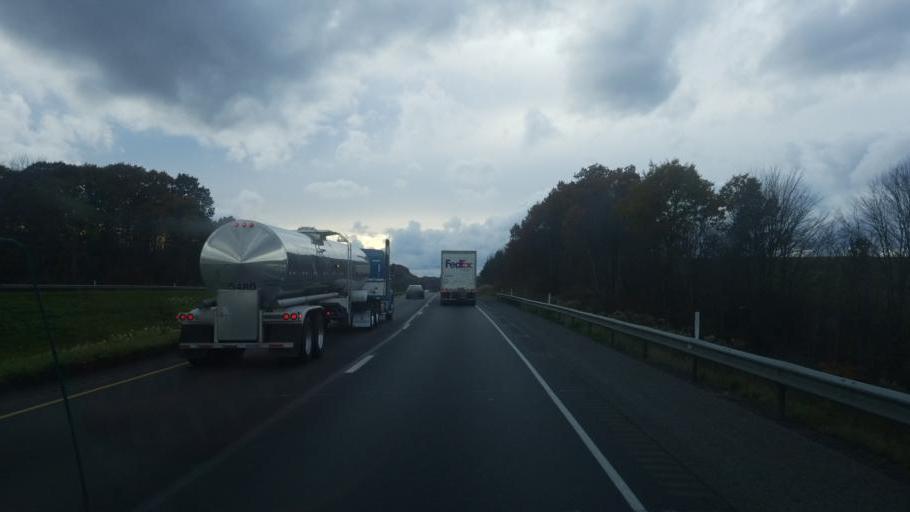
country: US
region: Pennsylvania
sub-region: Venango County
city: Franklin
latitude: 41.1958
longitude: -79.8331
